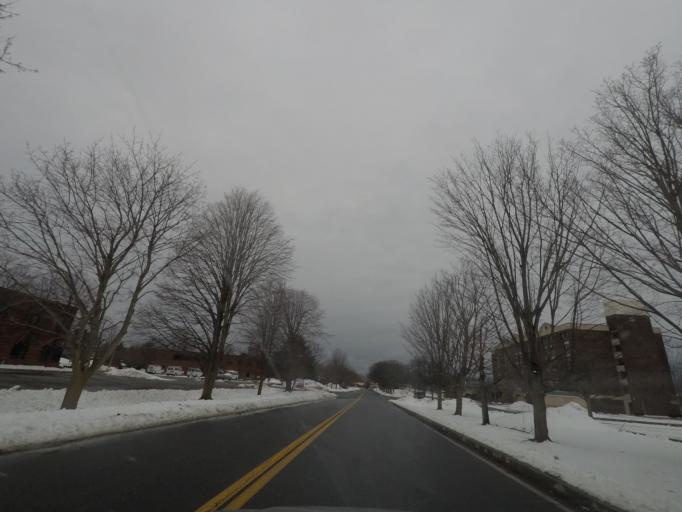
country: US
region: New York
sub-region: Albany County
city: Roessleville
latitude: 42.7216
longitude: -73.7973
